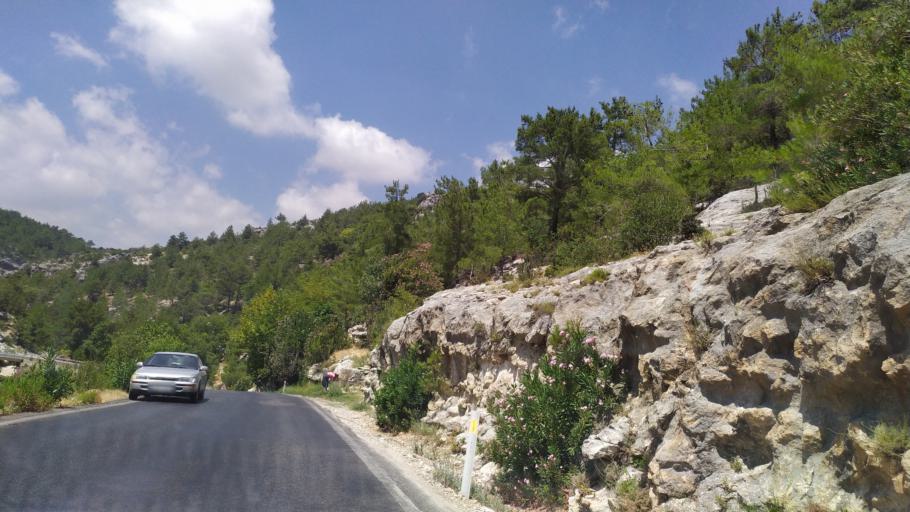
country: TR
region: Mersin
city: Gulnar
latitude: 36.2772
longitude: 33.3816
